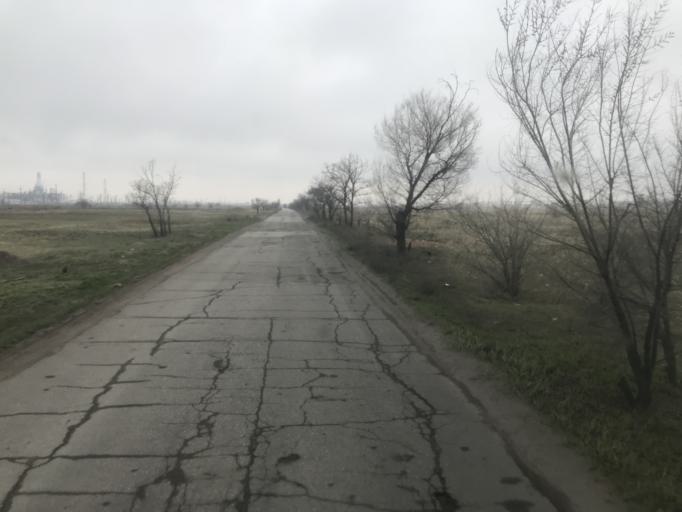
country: RU
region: Volgograd
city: Svetlyy Yar
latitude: 48.4973
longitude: 44.6501
